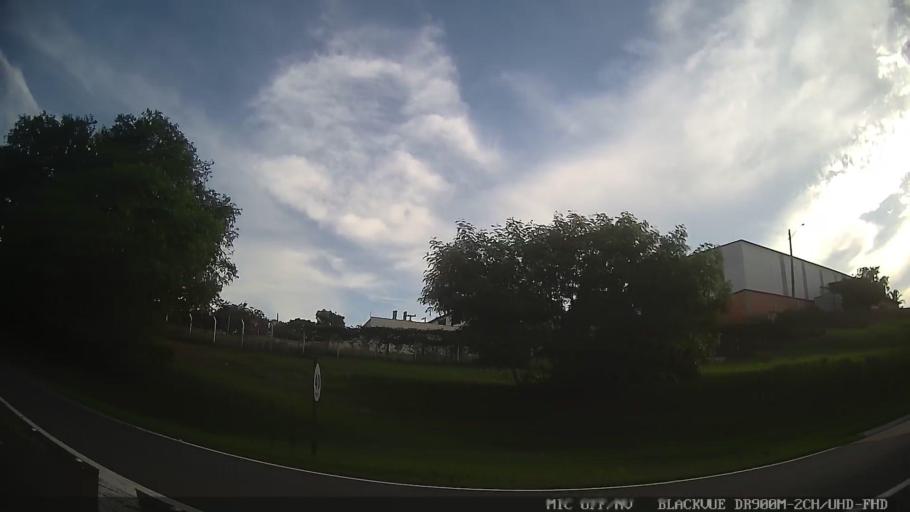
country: BR
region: Sao Paulo
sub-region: Tiete
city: Tiete
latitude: -23.1186
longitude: -47.7125
